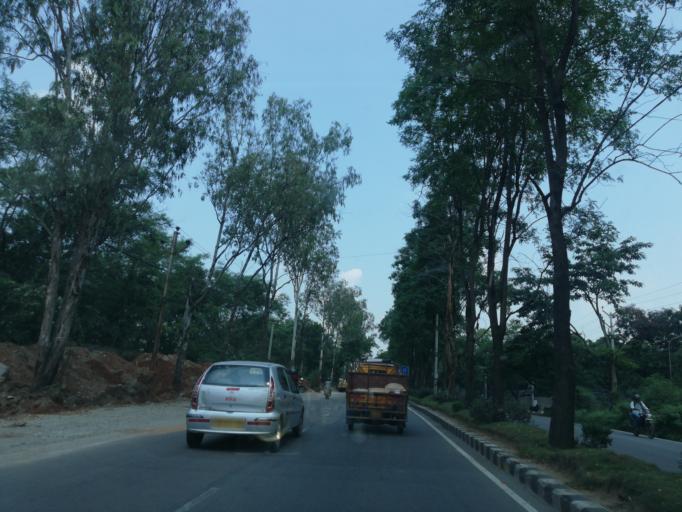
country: IN
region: Telangana
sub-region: Medak
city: Serilingampalle
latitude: 17.4533
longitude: 78.3431
